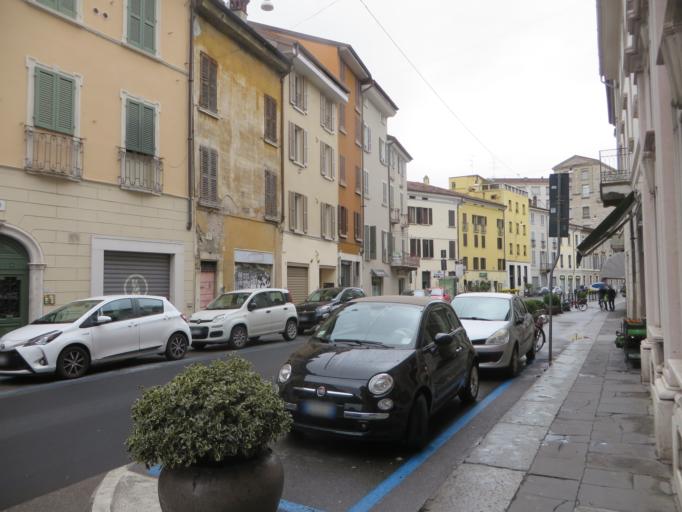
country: IT
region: Lombardy
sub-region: Provincia di Brescia
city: Brescia
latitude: 45.5364
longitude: 10.2139
